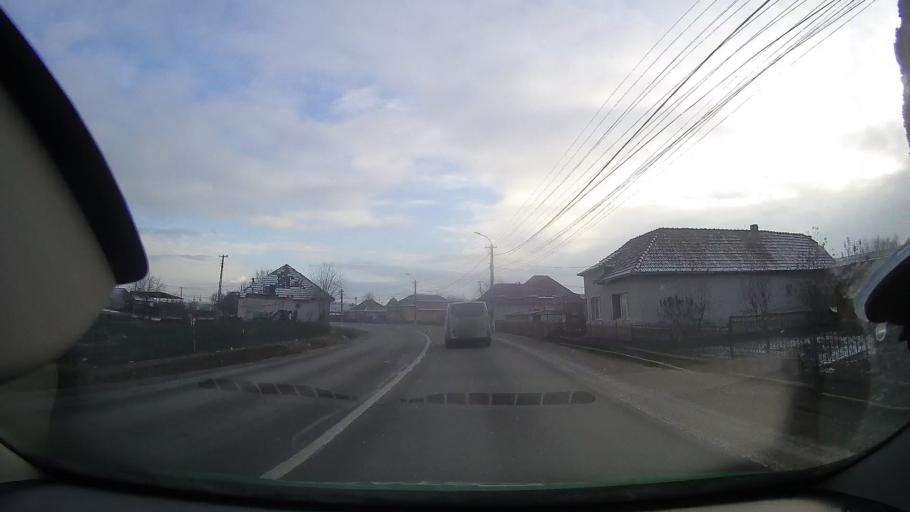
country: RO
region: Mures
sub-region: Comuna Cuci
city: Cuci
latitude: 46.4642
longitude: 24.1503
